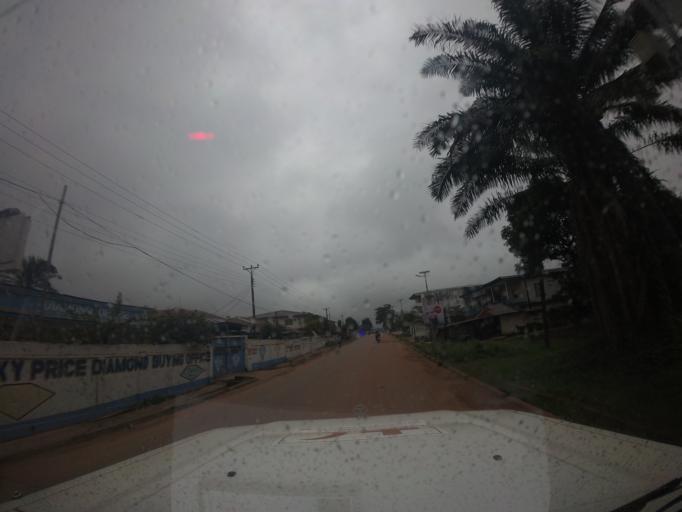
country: SL
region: Eastern Province
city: Kenema
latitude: 7.8857
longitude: -11.1887
